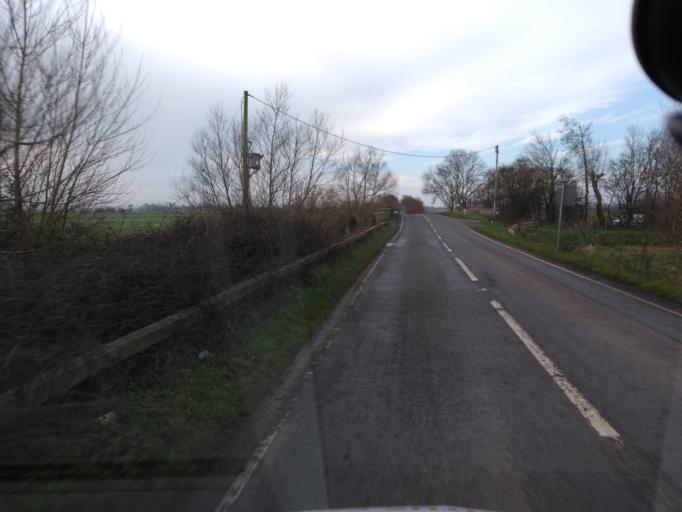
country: GB
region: England
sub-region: Somerset
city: Westonzoyland
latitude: 51.1065
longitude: -2.8607
